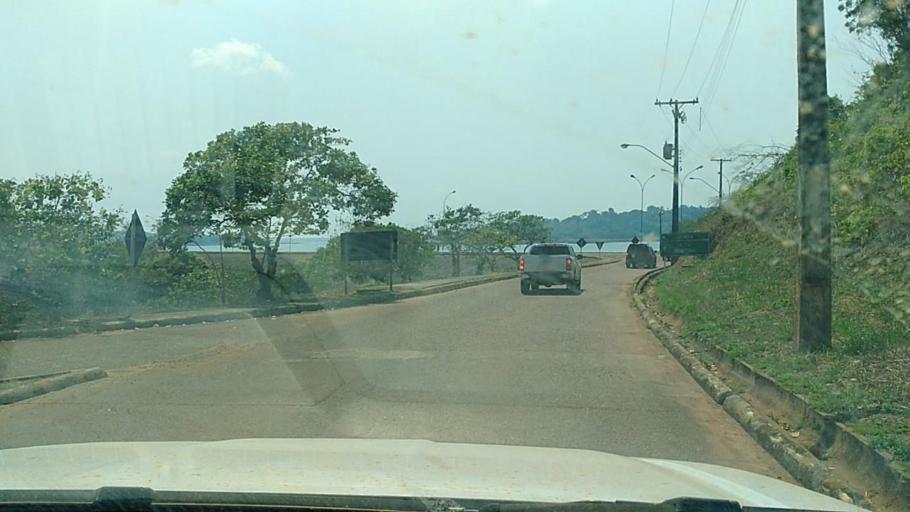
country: BR
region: Rondonia
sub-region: Porto Velho
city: Porto Velho
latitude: -8.7535
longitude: -63.4577
